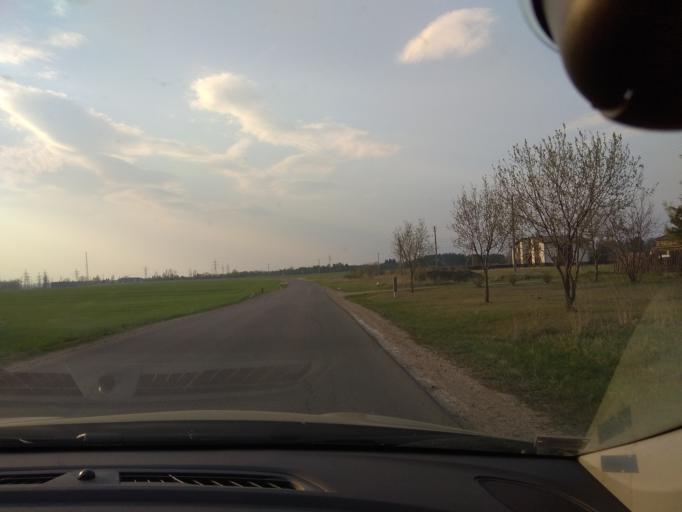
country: LT
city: Baltoji Voke
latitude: 54.6070
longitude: 25.1308
